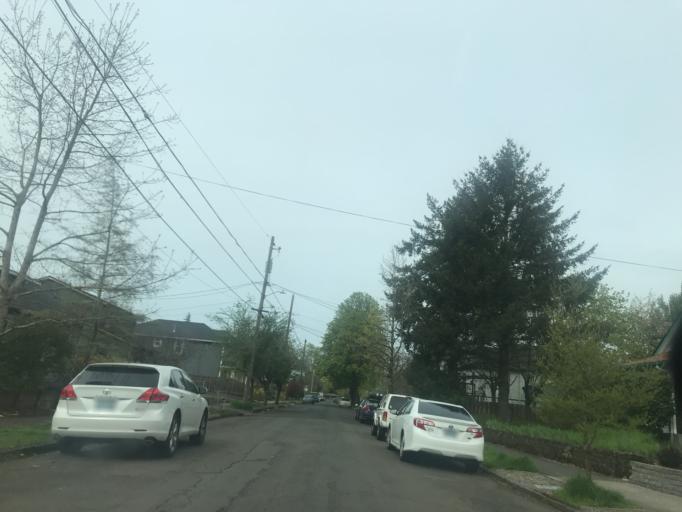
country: US
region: Oregon
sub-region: Multnomah County
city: Lents
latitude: 45.4910
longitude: -122.5895
